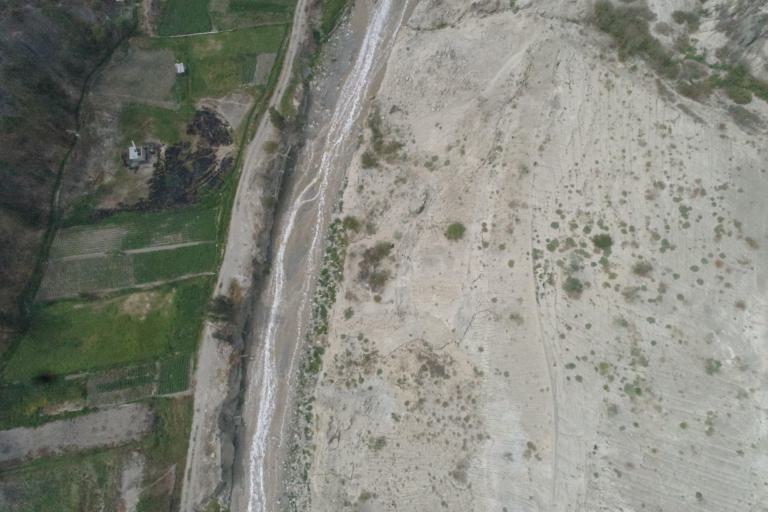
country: BO
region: La Paz
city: La Paz
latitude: -16.5989
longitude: -68.0664
